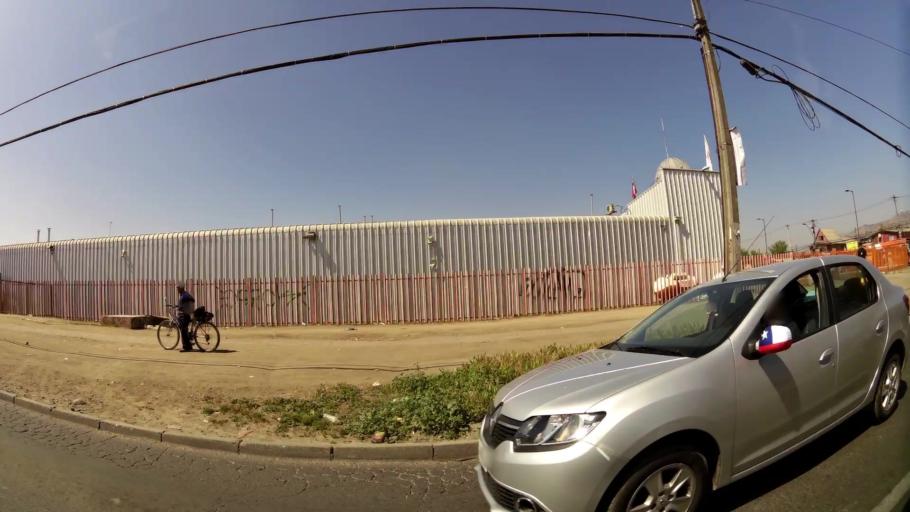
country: CL
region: Santiago Metropolitan
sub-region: Provincia de Santiago
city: Lo Prado
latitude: -33.3627
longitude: -70.7366
